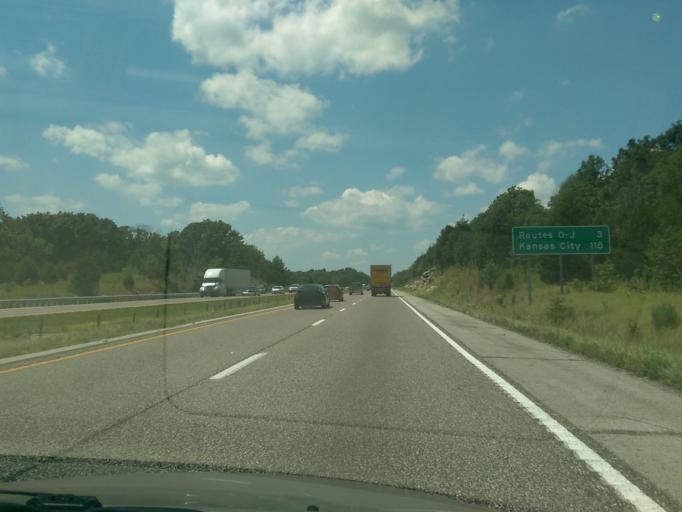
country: US
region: Missouri
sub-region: Boone County
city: Columbia
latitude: 38.9724
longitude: -92.4492
